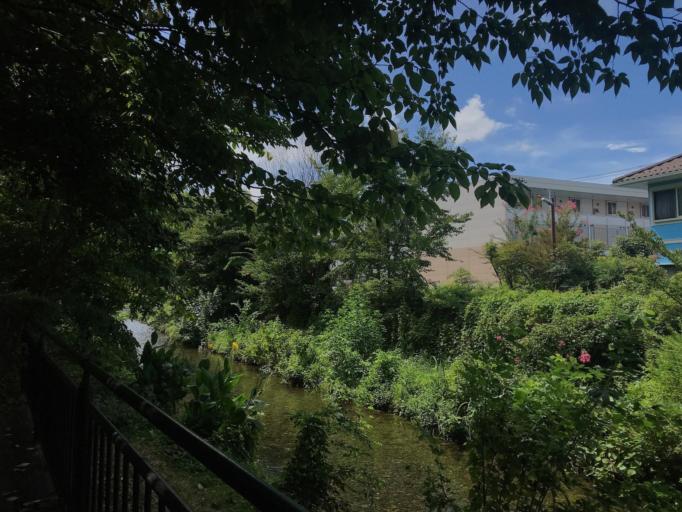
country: JP
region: Tokyo
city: Tanashicho
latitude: 35.7546
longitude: 139.5307
